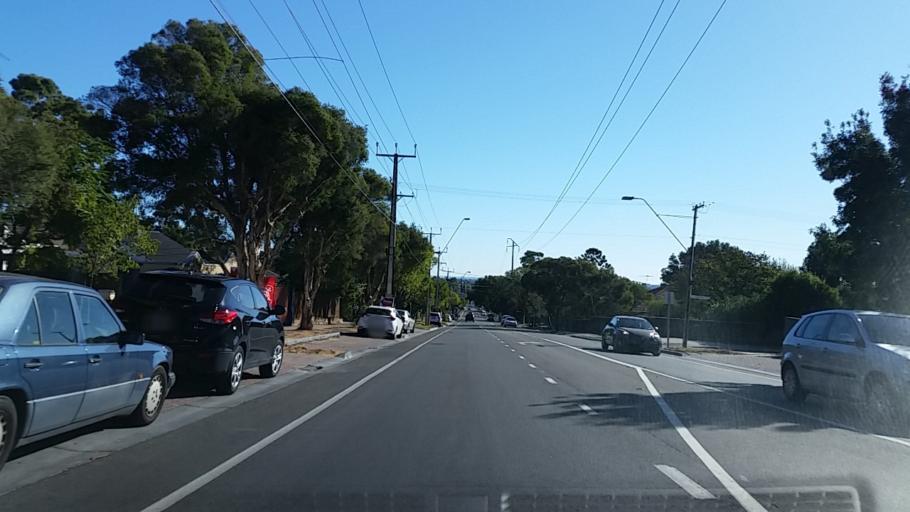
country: AU
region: South Australia
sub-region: Mitcham
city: Clapham
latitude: -34.9902
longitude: 138.6056
